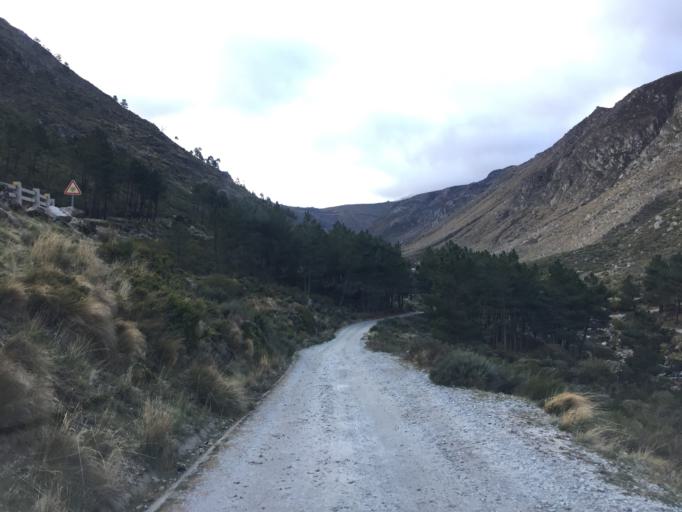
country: PT
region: Guarda
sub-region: Manteigas
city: Manteigas
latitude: 40.3587
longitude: -7.5561
